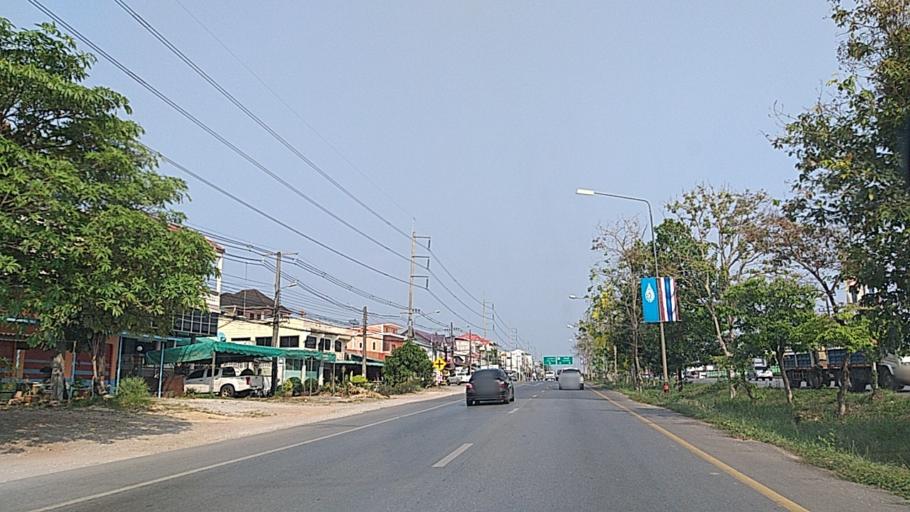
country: TH
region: Rayong
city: Klaeng
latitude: 12.7782
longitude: 101.7065
